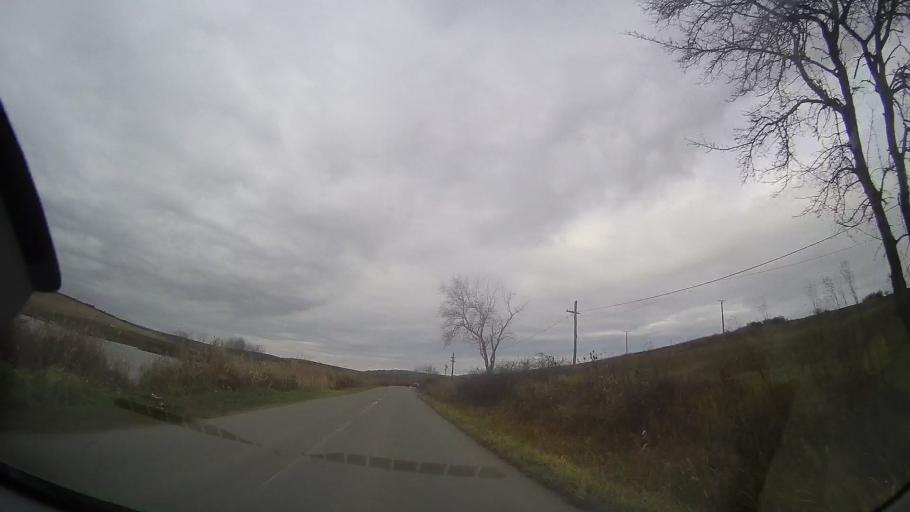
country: RO
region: Mures
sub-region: Comuna Faragau
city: Faragau
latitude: 46.7446
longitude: 24.5331
